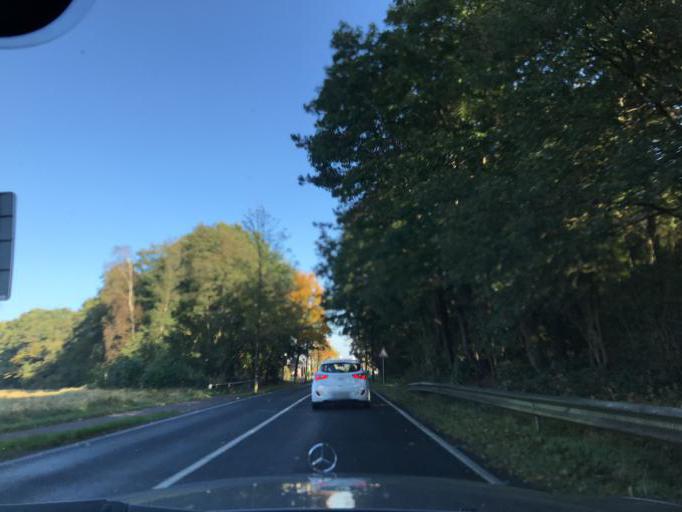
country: DE
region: Lower Saxony
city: Papenburg
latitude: 53.0822
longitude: 7.3799
